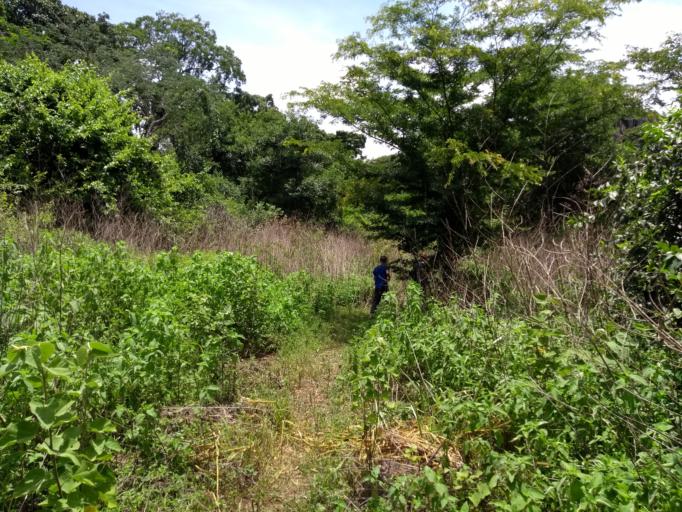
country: BR
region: Goias
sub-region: Formosa
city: Formosa
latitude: -15.4971
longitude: -47.3012
